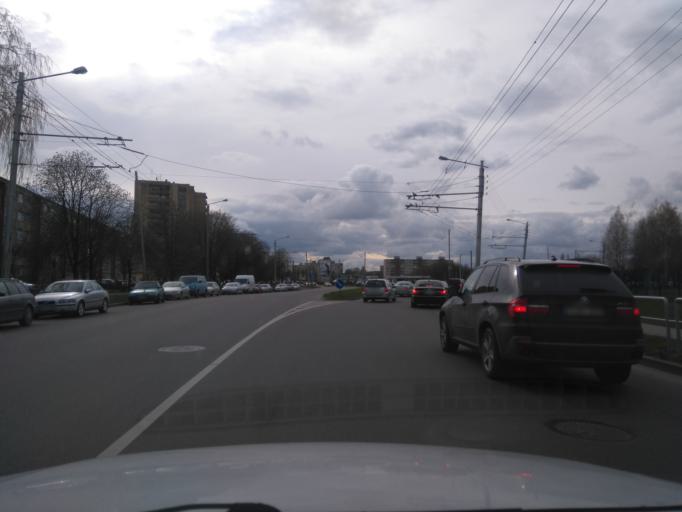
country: LT
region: Kauno apskritis
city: Dainava (Kaunas)
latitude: 54.9115
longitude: 23.9777
